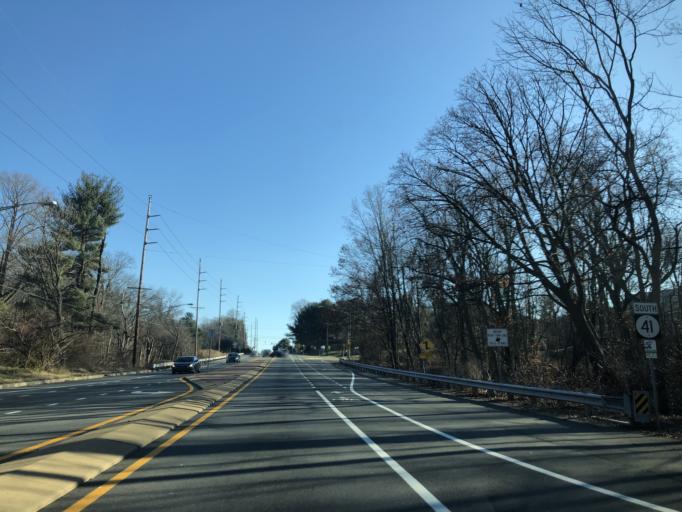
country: US
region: Delaware
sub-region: New Castle County
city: Hockessin
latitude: 39.7797
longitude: -75.6794
